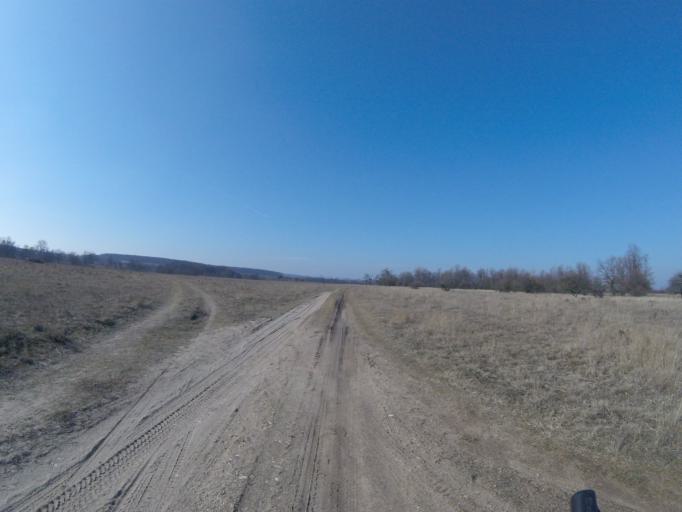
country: HU
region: Komarom-Esztergom
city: Oroszlany
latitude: 47.4619
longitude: 18.3499
